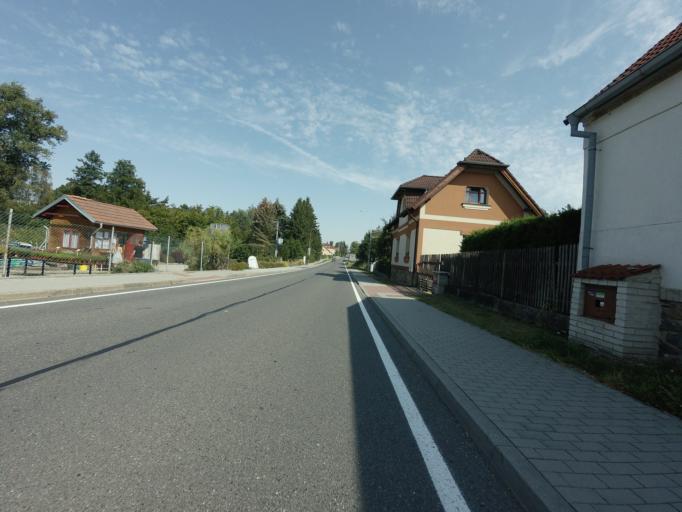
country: CZ
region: Jihocesky
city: Bernartice
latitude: 49.3700
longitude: 14.3796
